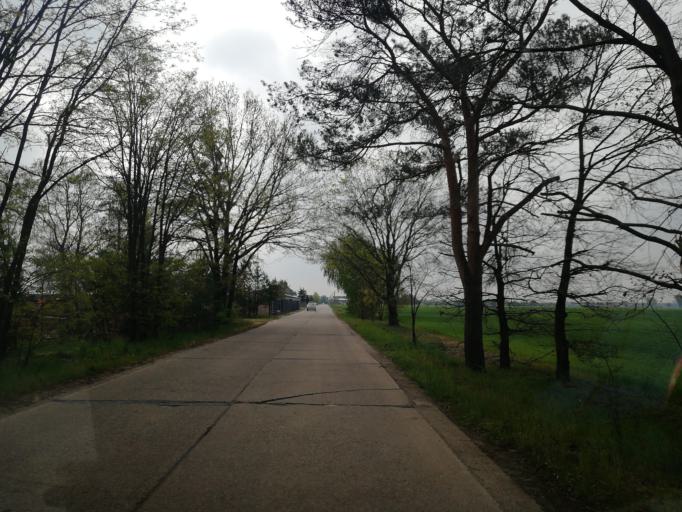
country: DE
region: Saxony
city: Beilrode
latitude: 51.6536
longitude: 13.1149
